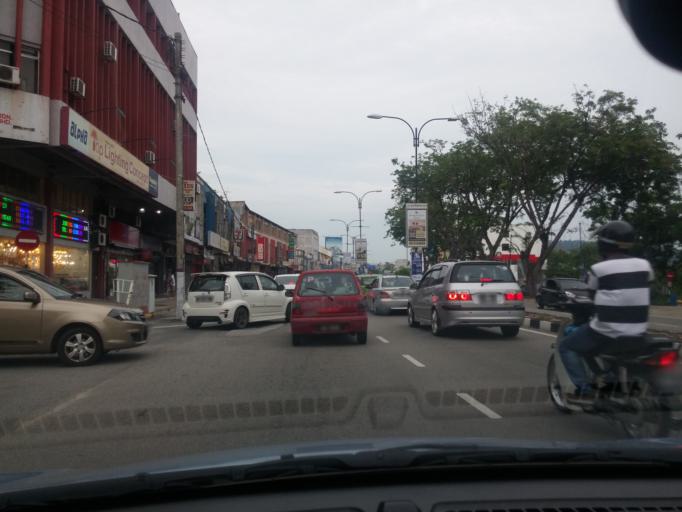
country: MY
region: Pahang
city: Kuantan
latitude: 3.8102
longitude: 103.3313
